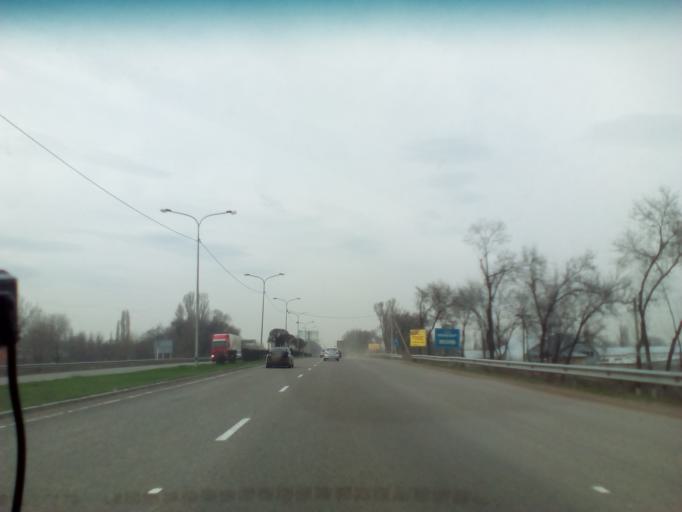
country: KZ
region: Almaty Oblysy
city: Burunday
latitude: 43.2187
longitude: 76.6447
